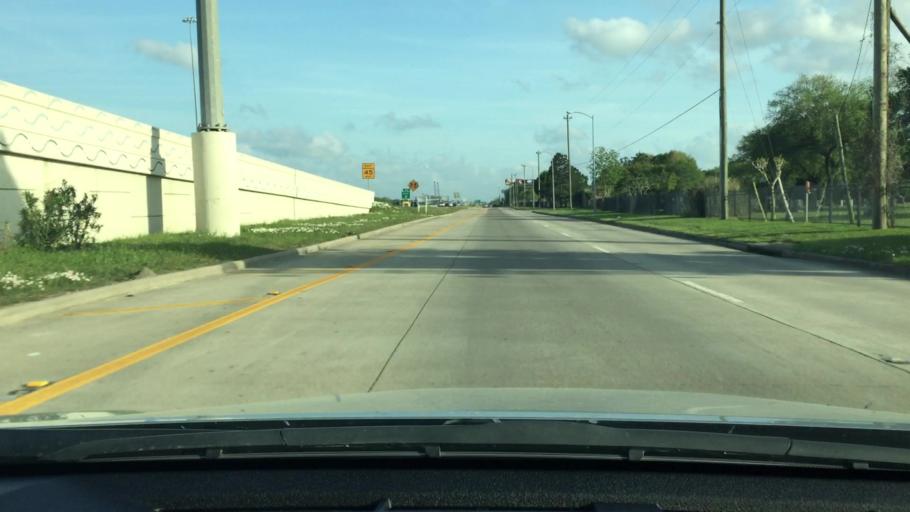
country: US
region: Texas
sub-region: Harris County
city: Webster
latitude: 29.5191
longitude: -95.1241
